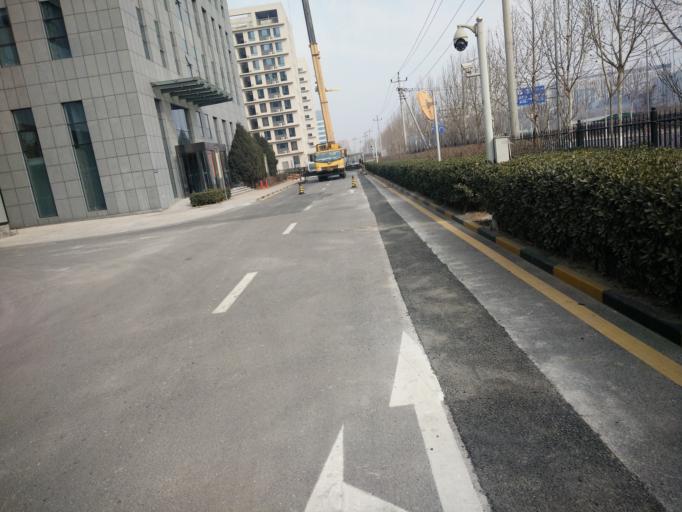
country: CN
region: Beijing
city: Jiugong
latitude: 39.7593
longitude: 116.5109
